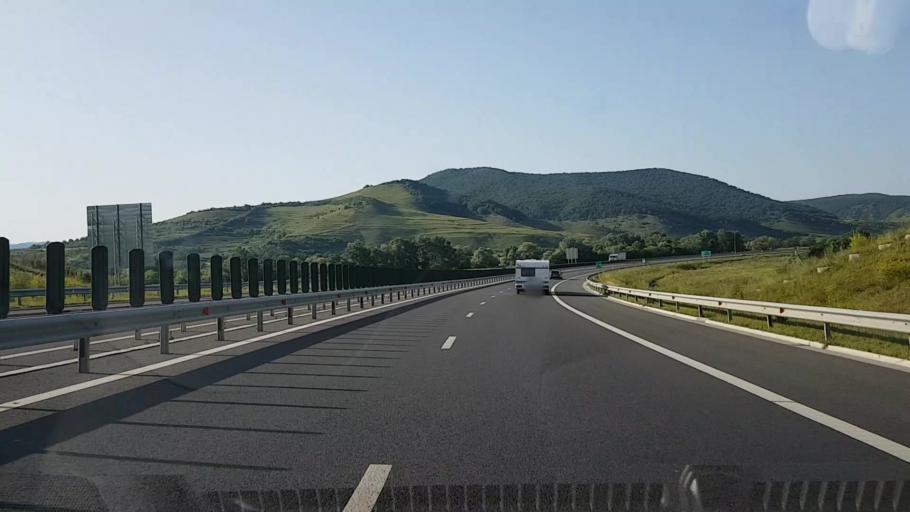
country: RO
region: Alba
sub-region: Comuna Miraslau
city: Miraslau
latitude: 46.3518
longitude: 23.7241
